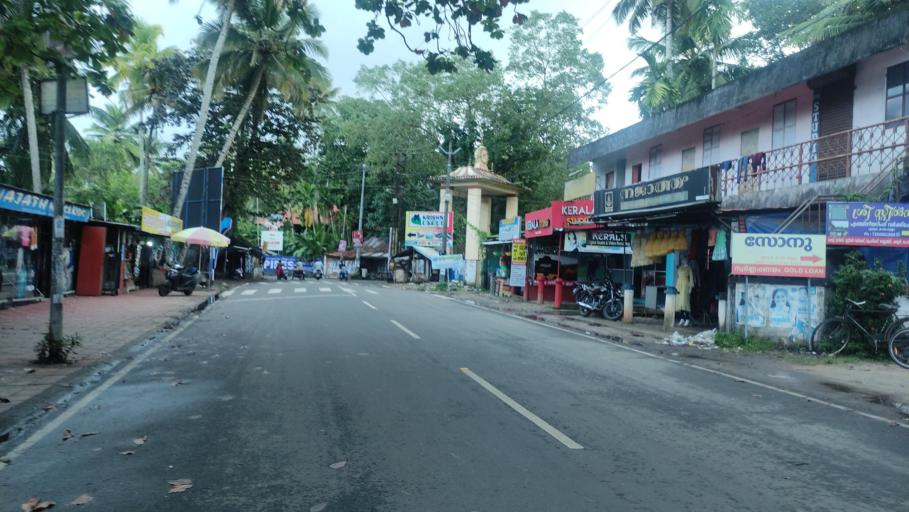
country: IN
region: Kerala
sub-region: Alappuzha
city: Kayankulam
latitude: 9.1937
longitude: 76.4998
